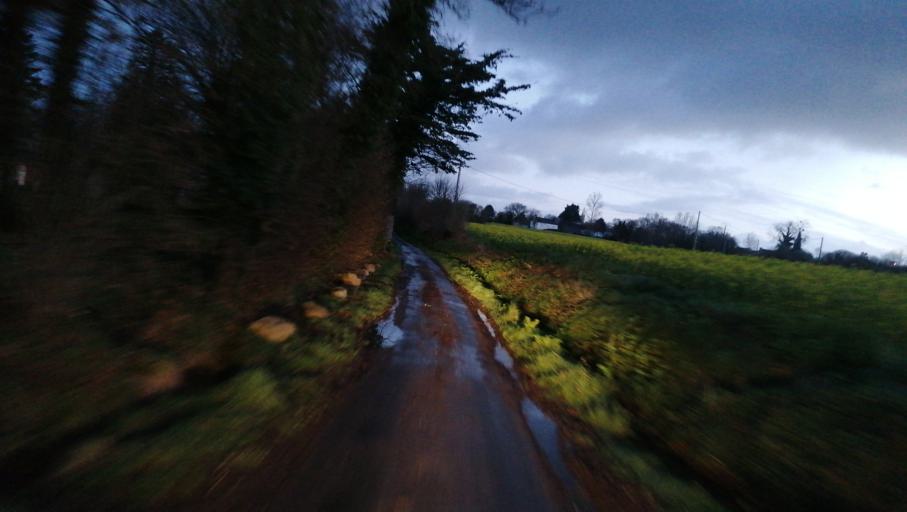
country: FR
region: Brittany
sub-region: Departement des Cotes-d'Armor
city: Plouha
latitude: 48.6664
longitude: -2.9656
